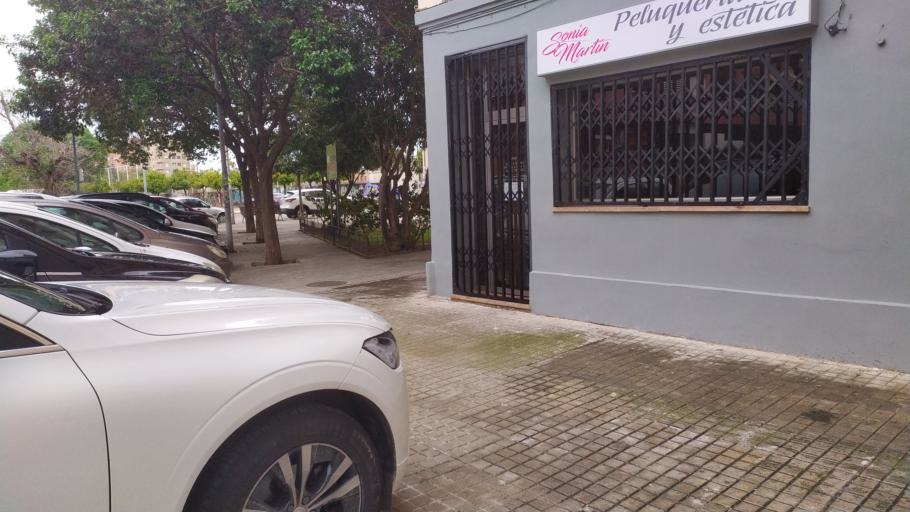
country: ES
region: Valencia
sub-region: Provincia de Valencia
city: Mislata
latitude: 39.4669
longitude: -0.4146
